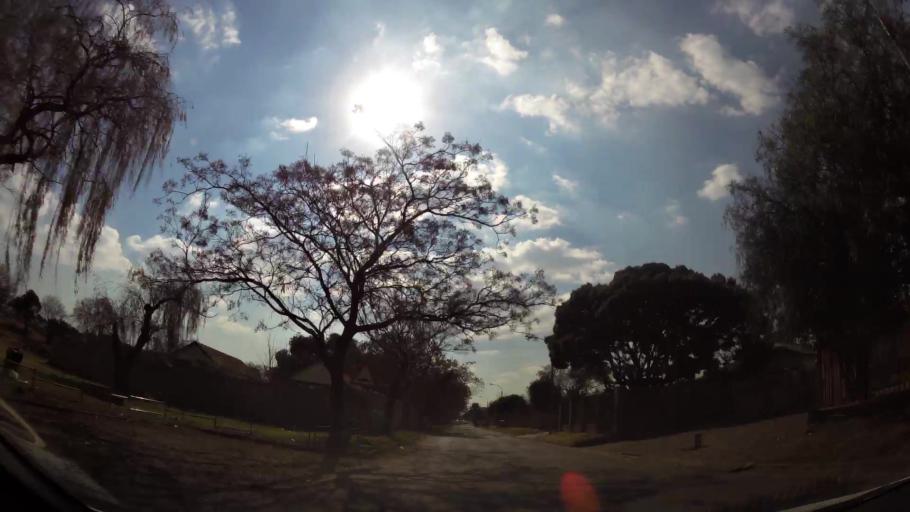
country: ZA
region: Gauteng
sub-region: Ekurhuleni Metropolitan Municipality
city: Germiston
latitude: -26.1857
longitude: 28.2030
